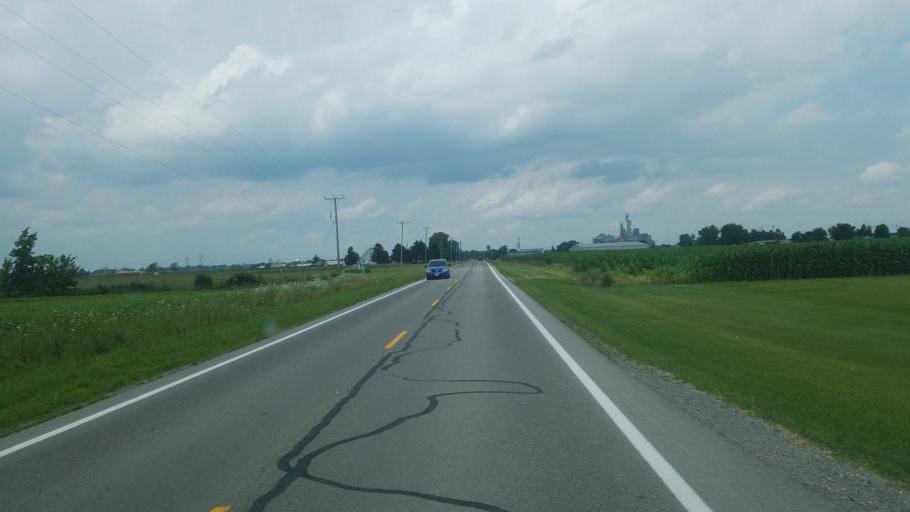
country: US
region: Ohio
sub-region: Hardin County
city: Kenton
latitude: 40.6202
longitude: -83.5971
